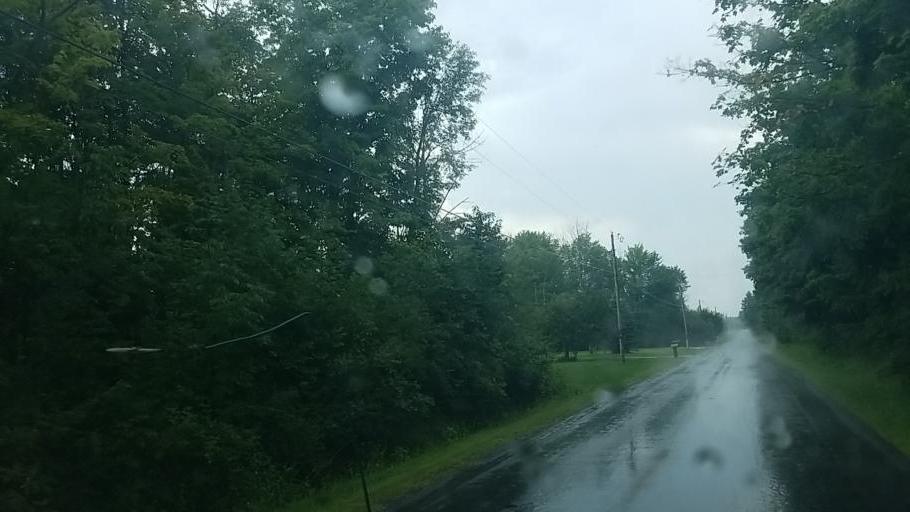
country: US
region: Ohio
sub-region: Lorain County
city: Grafton
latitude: 41.1584
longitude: -82.0330
